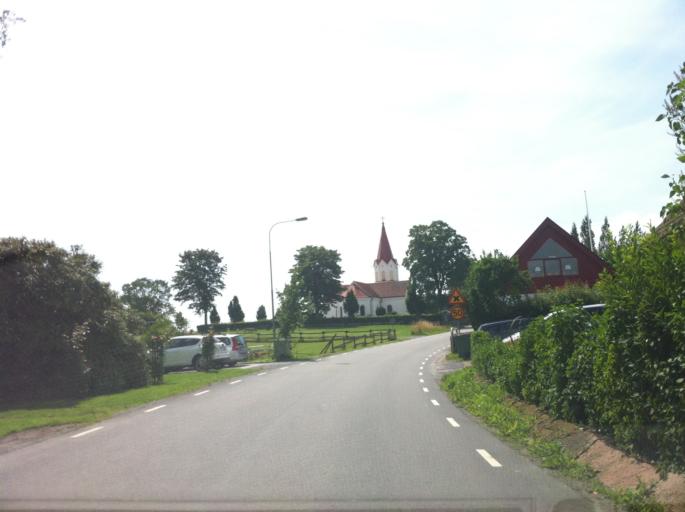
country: SE
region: Skane
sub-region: Skurups Kommun
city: Skurup
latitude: 55.4191
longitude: 13.4646
